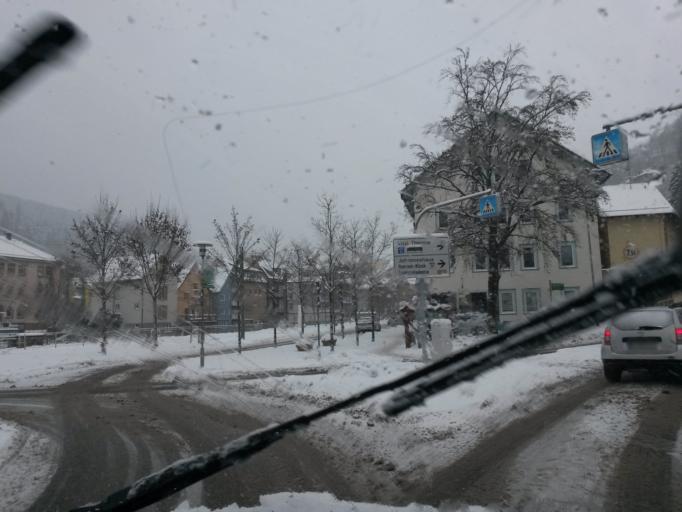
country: DE
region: Baden-Wuerttemberg
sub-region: Karlsruhe Region
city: Bad Wildbad
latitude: 48.7535
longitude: 8.5497
